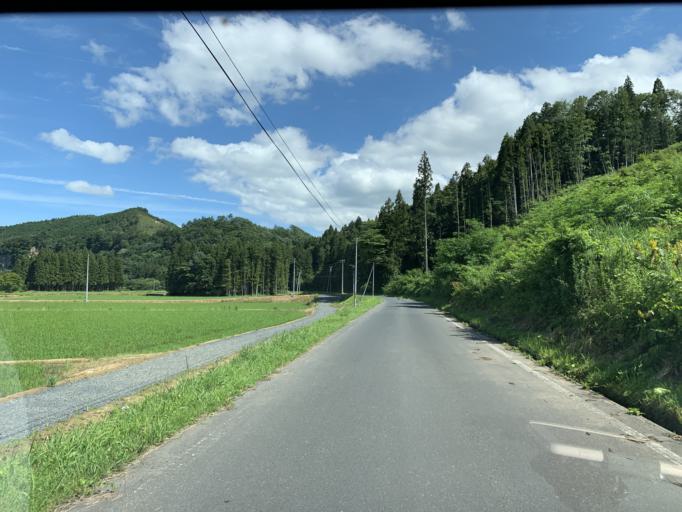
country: JP
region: Iwate
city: Ichinoseki
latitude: 38.9710
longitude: 140.9475
